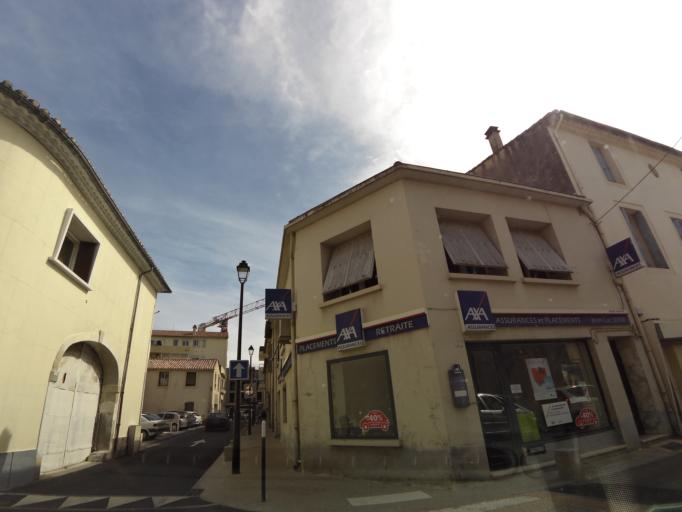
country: FR
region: Languedoc-Roussillon
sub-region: Departement de l'Herault
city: Lunel
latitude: 43.6780
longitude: 4.1345
